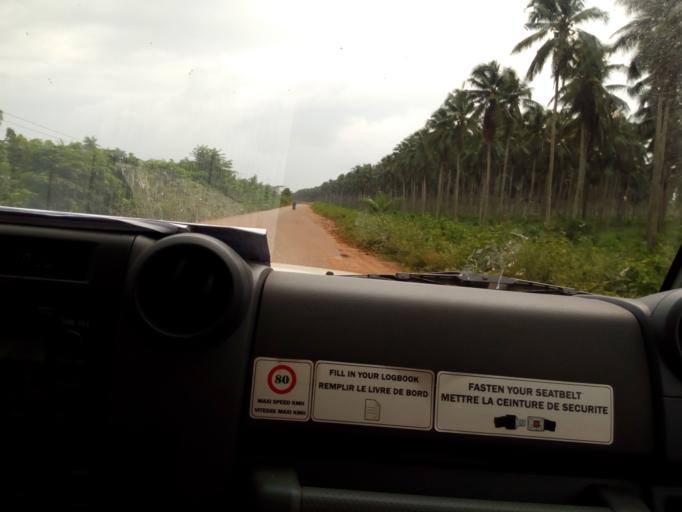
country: CI
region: Bas-Sassandra
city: Tabou
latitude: 4.5300
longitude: -7.2346
